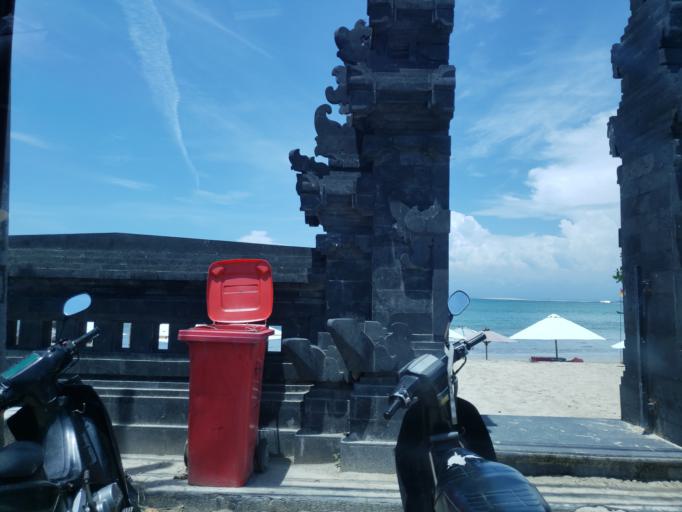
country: ID
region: Bali
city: Jimbaran
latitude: -8.7815
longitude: 115.1636
